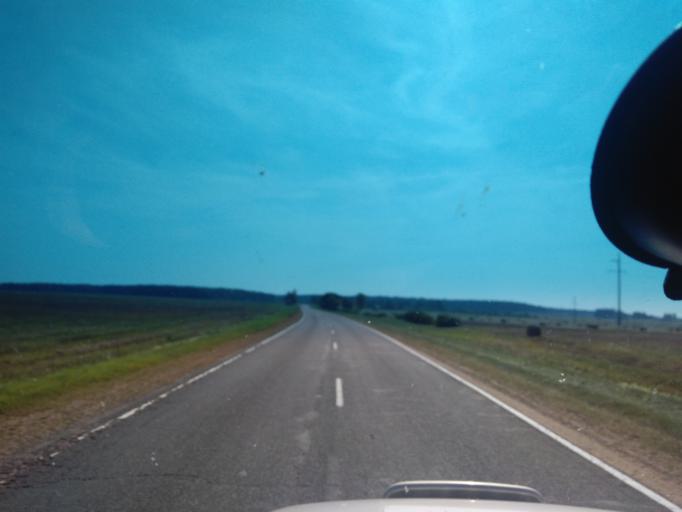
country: BY
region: Minsk
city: Uzda
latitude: 53.3945
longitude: 27.2341
